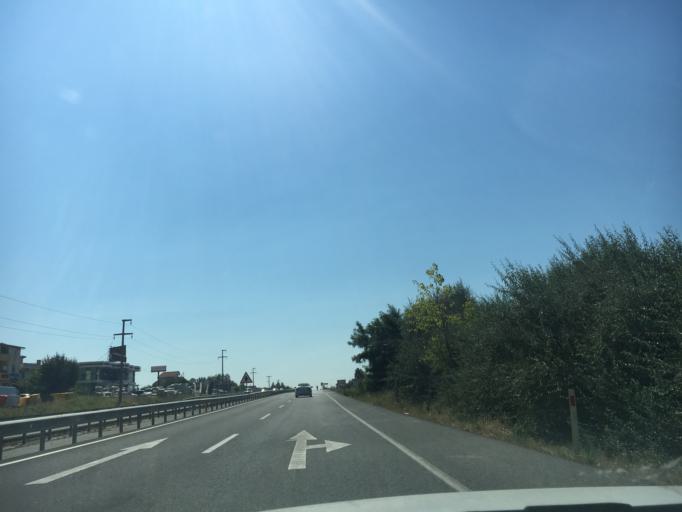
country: TR
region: Tekirdag
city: Marmara Ereglisi
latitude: 40.9764
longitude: 27.8736
